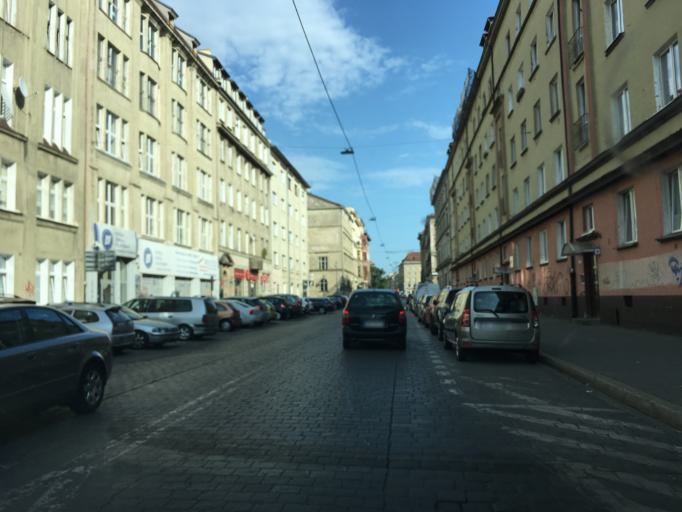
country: PL
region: Lower Silesian Voivodeship
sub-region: Powiat wroclawski
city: Wroclaw
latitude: 51.1036
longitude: 17.0263
